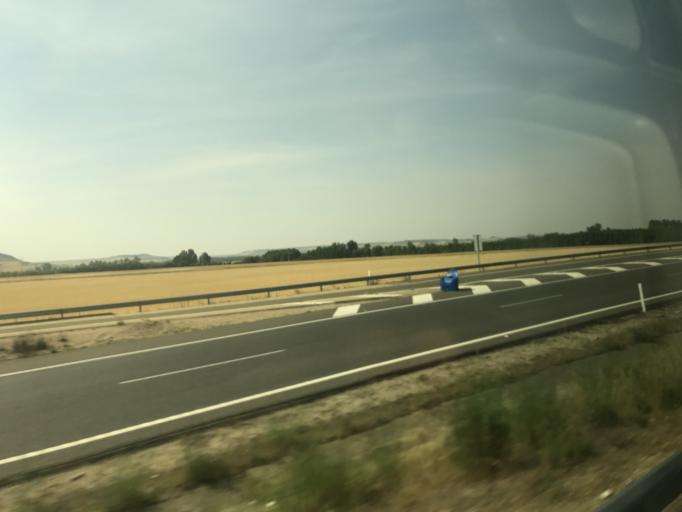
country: ES
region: Castille and Leon
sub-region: Provincia de Palencia
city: Palenzuela
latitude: 42.1189
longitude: -4.1523
